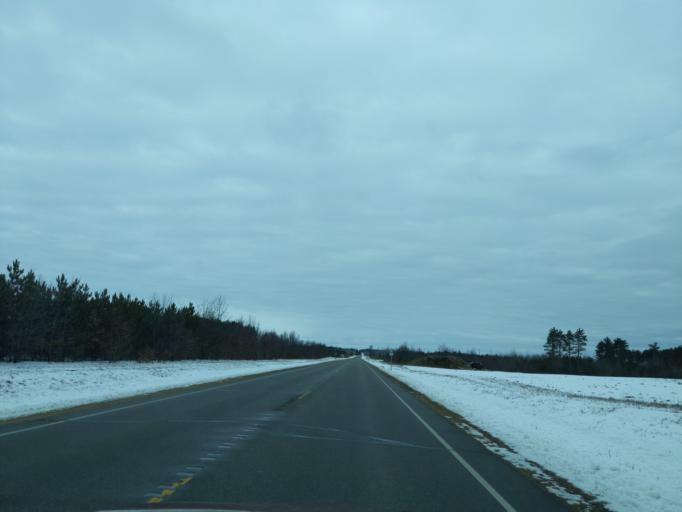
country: US
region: Wisconsin
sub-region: Waushara County
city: Wautoma
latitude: 43.9788
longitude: -89.3276
